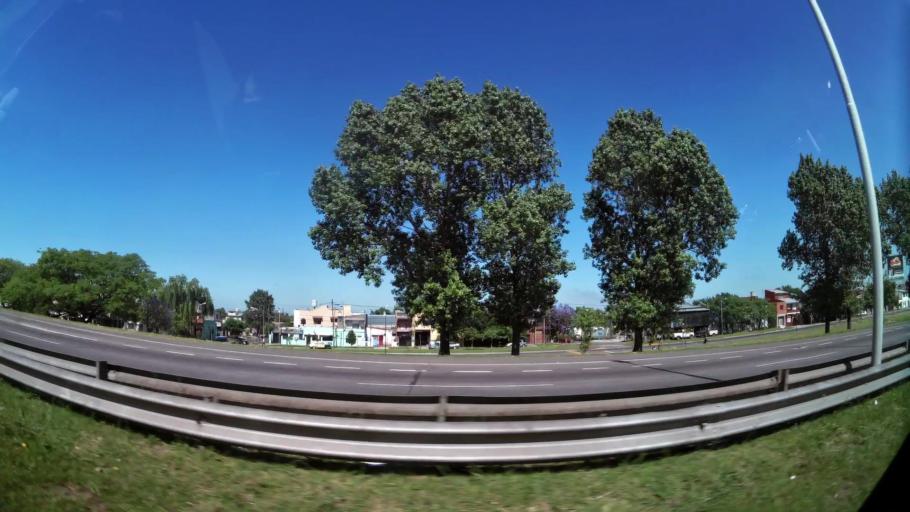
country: AR
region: Buenos Aires
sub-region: Partido de Tigre
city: Tigre
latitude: -34.4509
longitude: -58.5757
